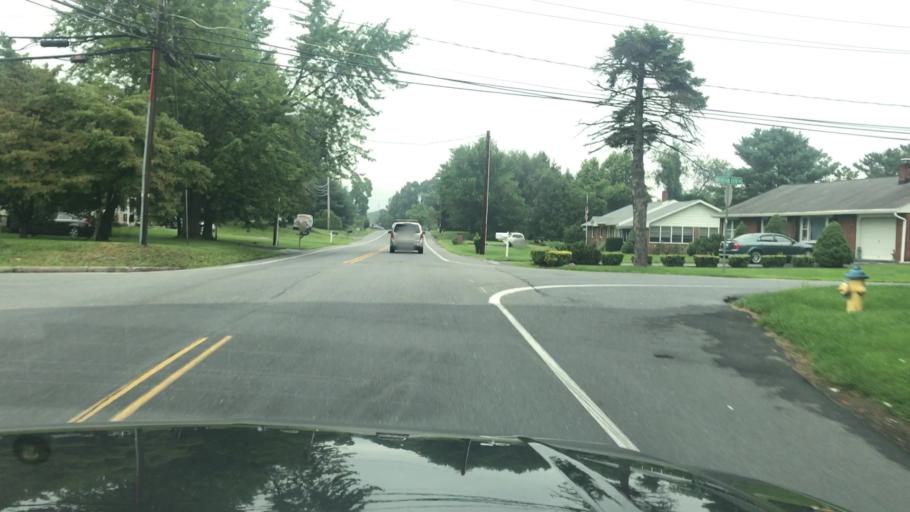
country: US
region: Pennsylvania
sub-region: Cumberland County
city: Enola
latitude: 40.2771
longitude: -76.9698
